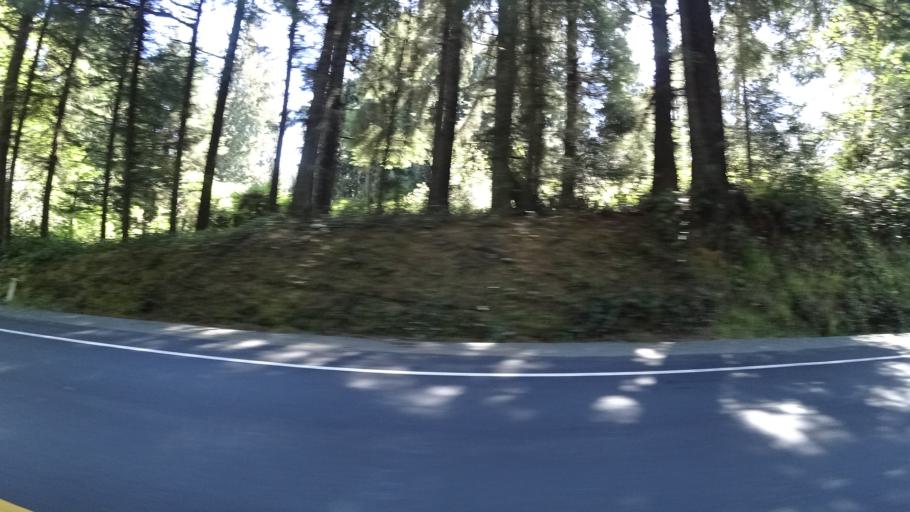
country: US
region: California
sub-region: Humboldt County
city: Westhaven-Moonstone
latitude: 41.1686
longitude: -124.1022
